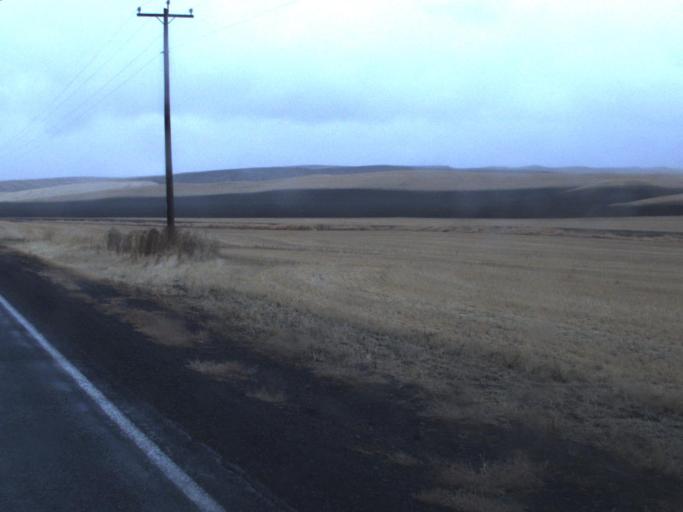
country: US
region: Washington
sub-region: Whitman County
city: Colfax
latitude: 47.0062
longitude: -117.4531
